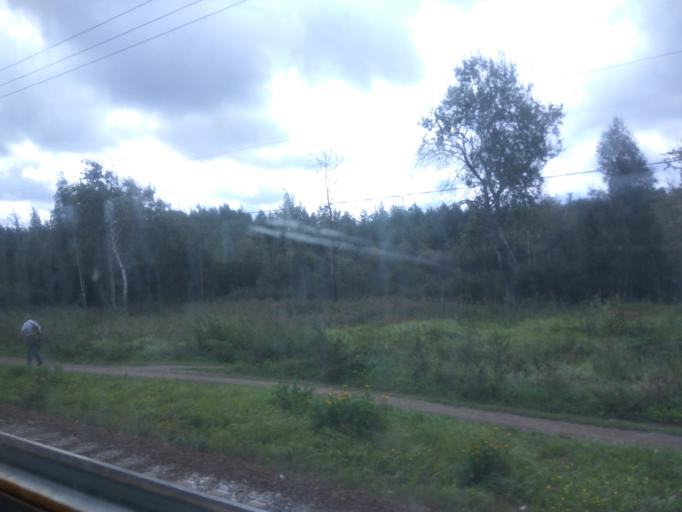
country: RU
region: Moskovskaya
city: Beloozerskiy
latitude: 55.4734
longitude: 38.4247
